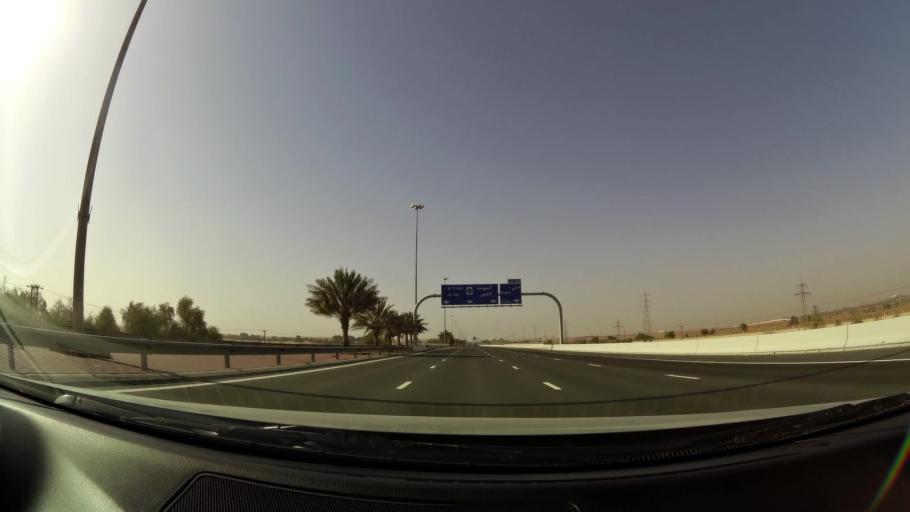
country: OM
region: Al Buraimi
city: Al Buraymi
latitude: 24.5030
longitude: 55.7674
